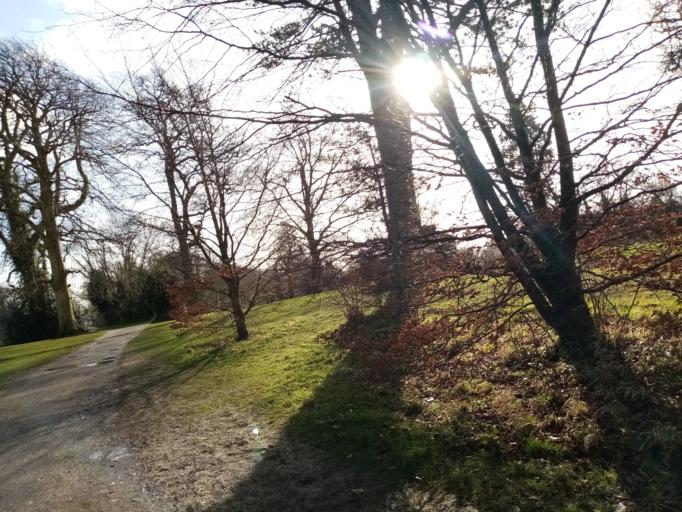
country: IE
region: Leinster
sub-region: Kildare
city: Celbridge
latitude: 53.3463
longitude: -6.5284
